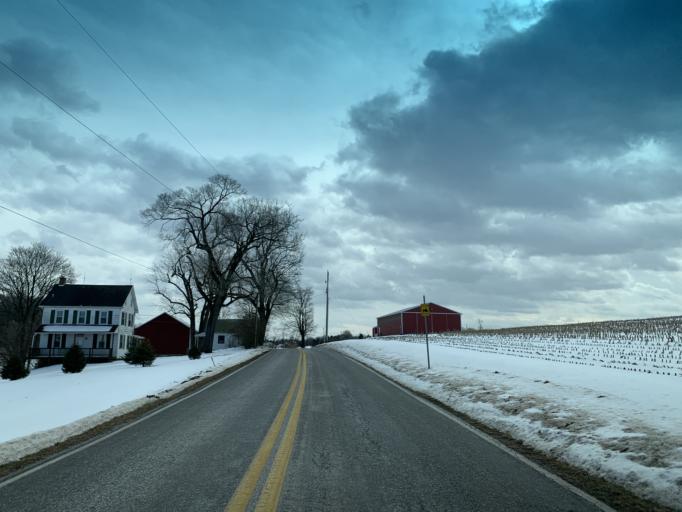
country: US
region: Pennsylvania
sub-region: York County
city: Shrewsbury
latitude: 39.7896
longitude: -76.6477
